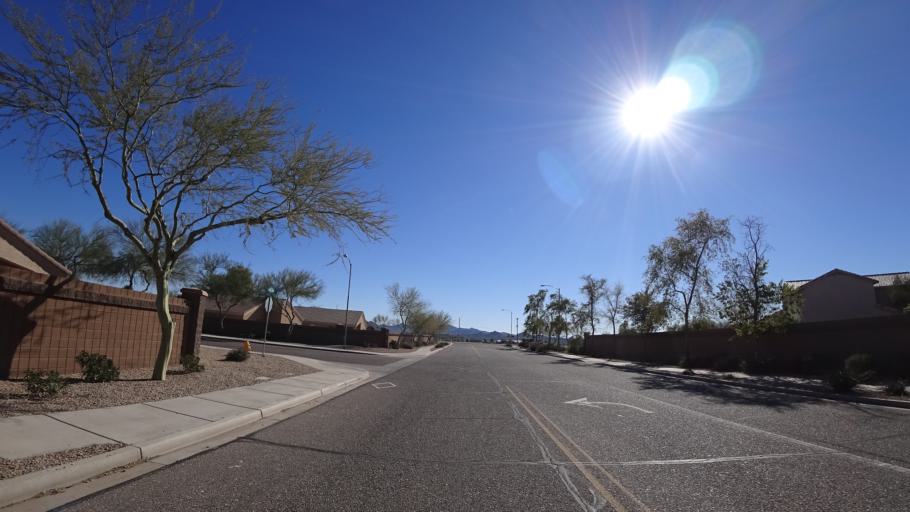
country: US
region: Arizona
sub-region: Maricopa County
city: Goodyear
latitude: 33.4147
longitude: -112.4051
